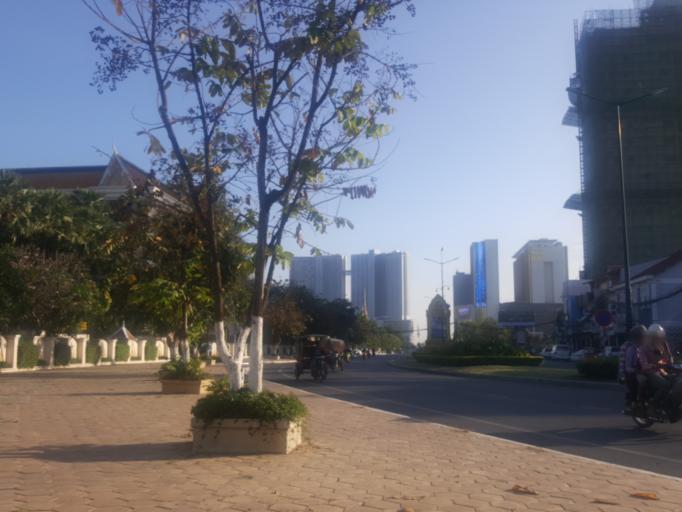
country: KH
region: Phnom Penh
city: Phnom Penh
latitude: 11.5617
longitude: 104.9352
